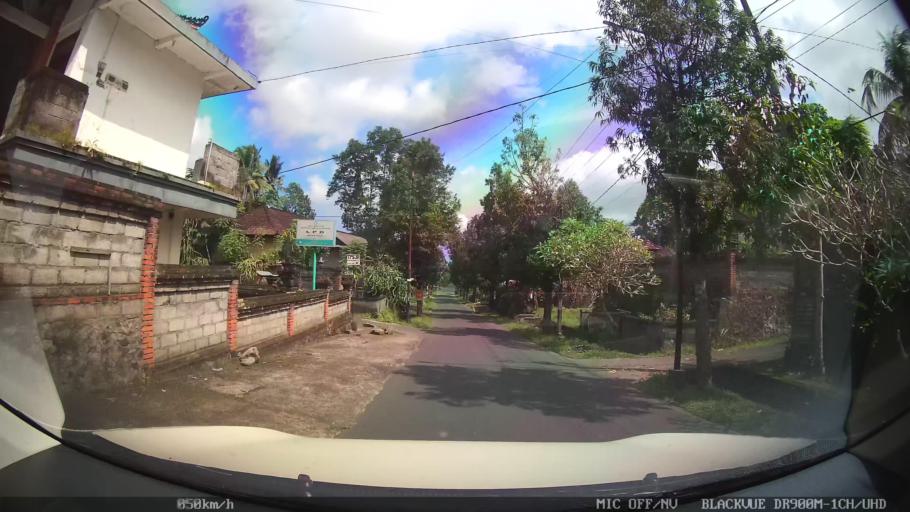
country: ID
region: Bali
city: Banjar Mulung
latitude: -8.4947
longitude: 115.3205
